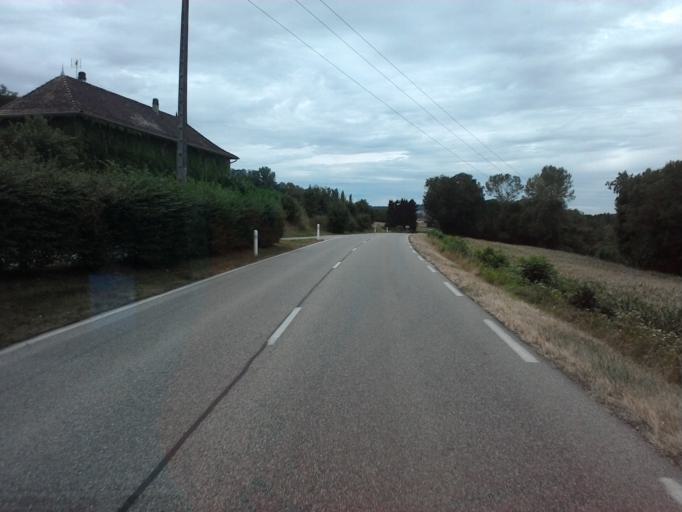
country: FR
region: Rhone-Alpes
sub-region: Departement de l'Isere
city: Thuellin
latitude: 45.6417
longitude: 5.5005
